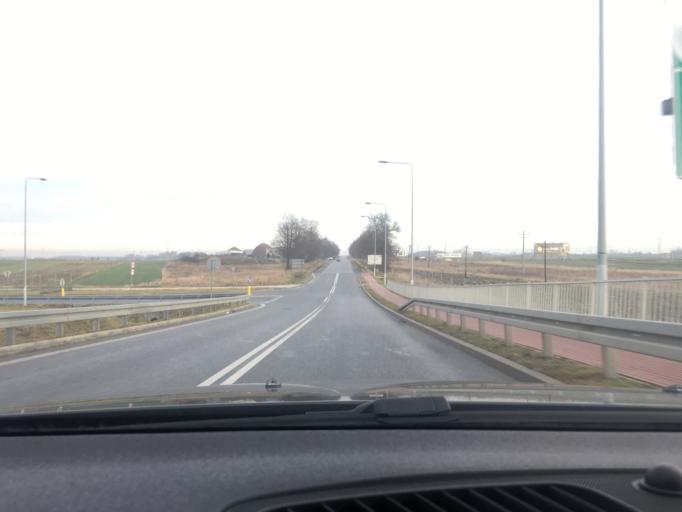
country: PL
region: Swietokrzyskie
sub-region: Powiat jedrzejowski
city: Jedrzejow
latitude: 50.6485
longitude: 20.3163
